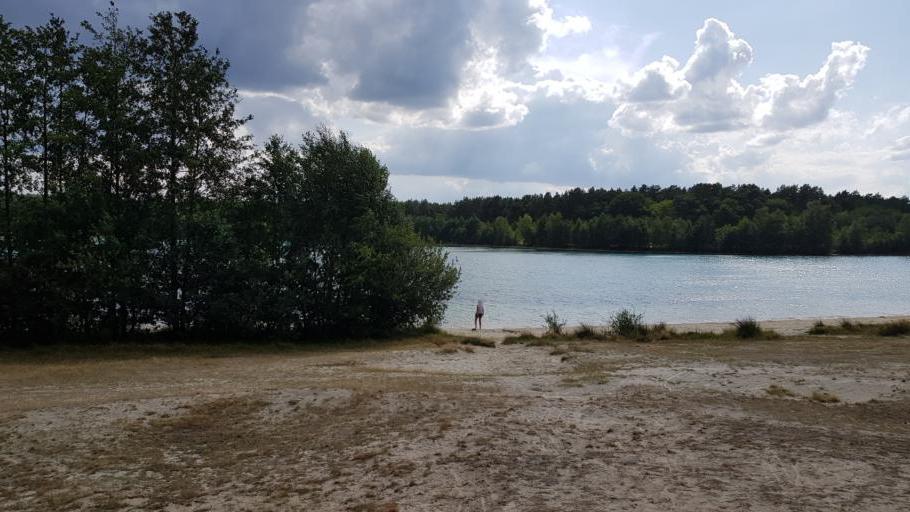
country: DE
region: Lower Saxony
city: Haren
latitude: 52.7983
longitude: 7.1839
